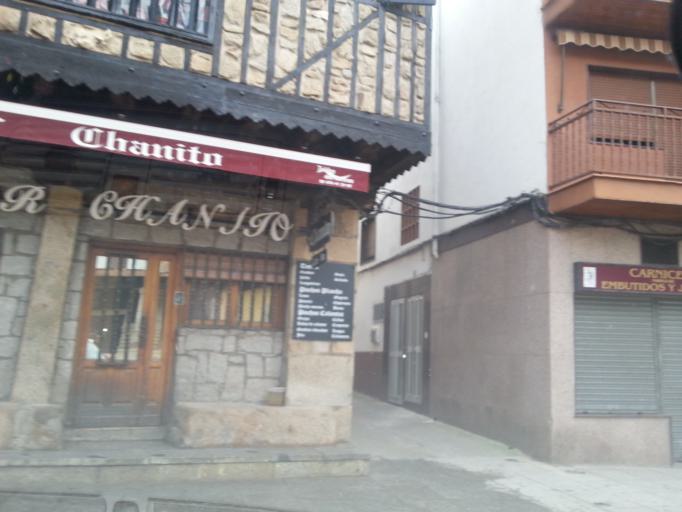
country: ES
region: Castille and Leon
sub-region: Provincia de Salamanca
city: Sotoserrano
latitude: 40.4374
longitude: -6.0332
